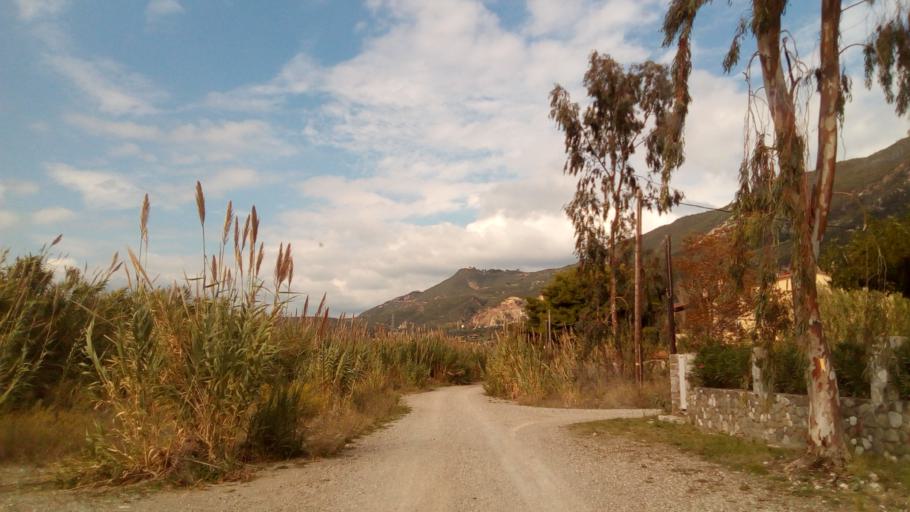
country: GR
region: West Greece
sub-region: Nomos Achaias
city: Kamarai
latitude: 38.3925
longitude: 21.9993
